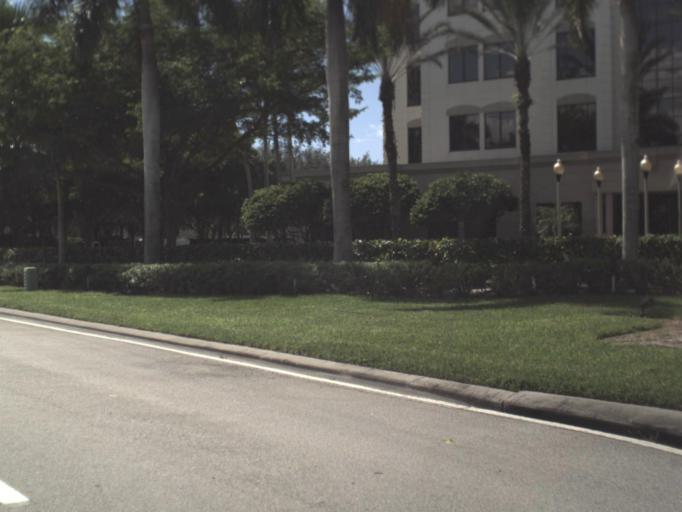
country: US
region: Florida
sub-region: Collier County
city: Pelican Bay
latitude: 26.2464
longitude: -81.8012
